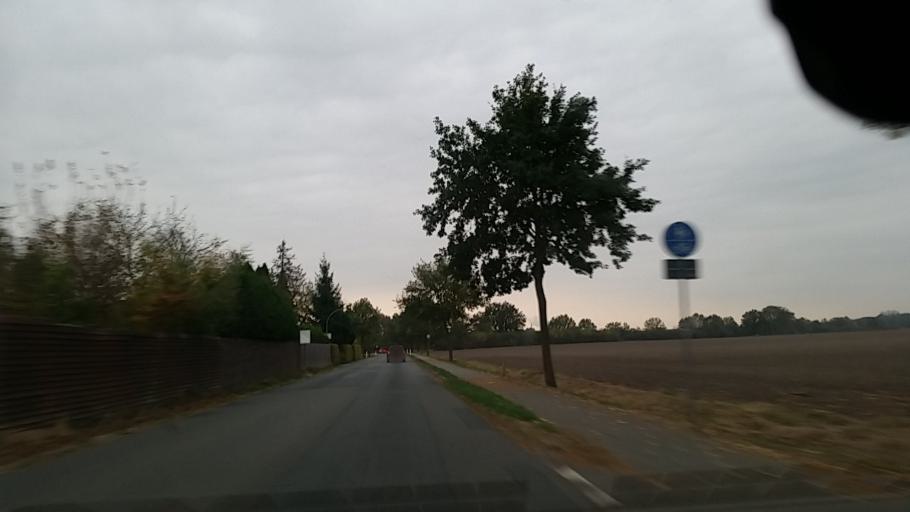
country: DE
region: Lower Saxony
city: Jembke
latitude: 52.4932
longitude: 10.7610
